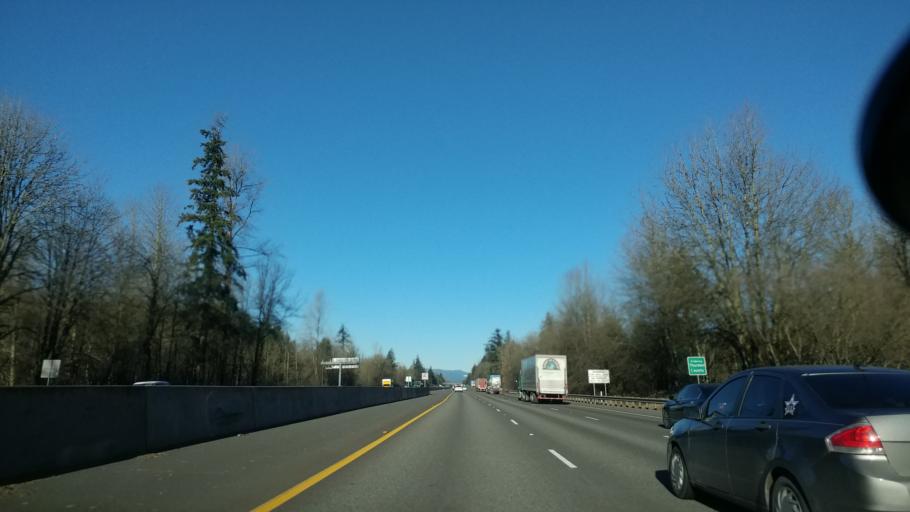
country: US
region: Washington
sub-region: Lewis County
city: Fords Prairie
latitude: 46.7640
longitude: -122.9919
